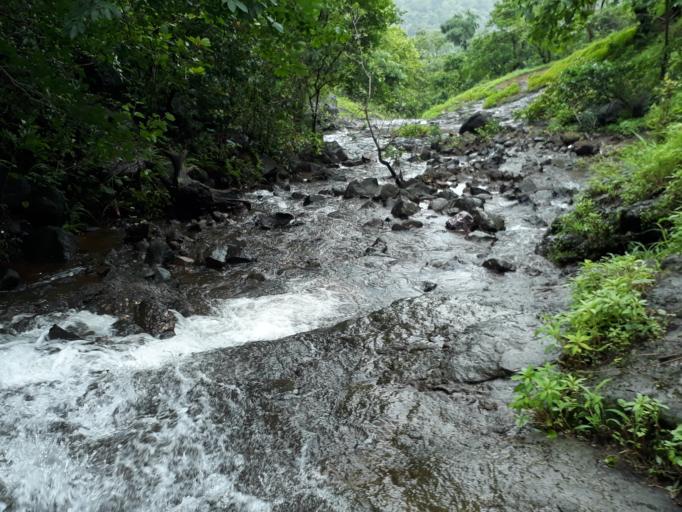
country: IN
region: Maharashtra
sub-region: Raigarh
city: Khopoli
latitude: 18.8412
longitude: 73.3822
